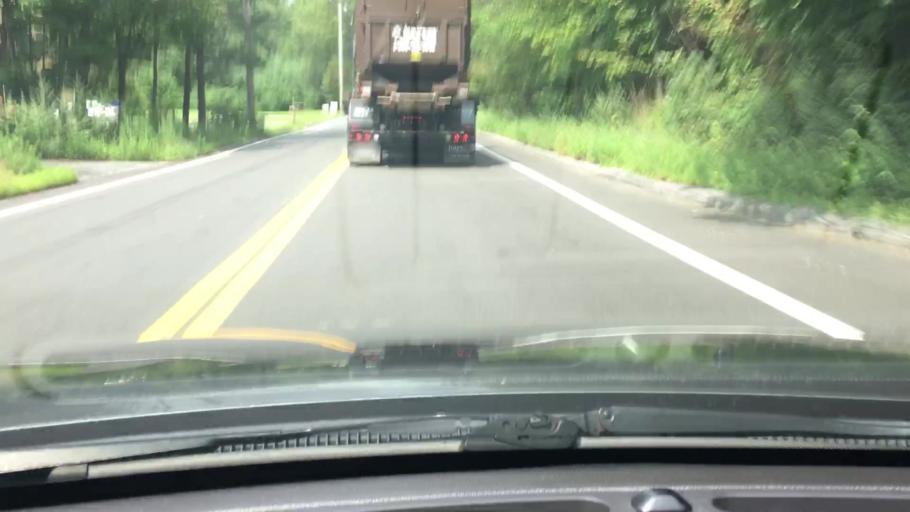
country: US
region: Massachusetts
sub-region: Worcester County
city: Westborough
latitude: 42.2455
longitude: -71.5820
